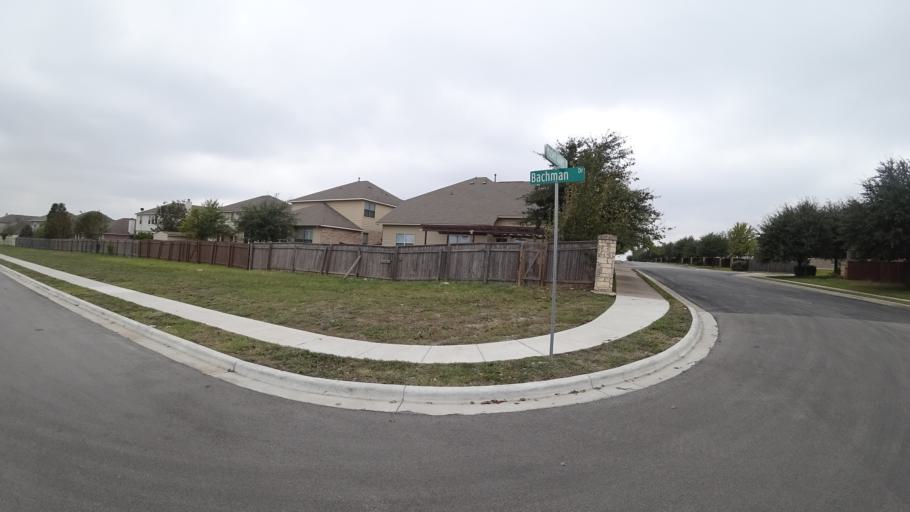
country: US
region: Texas
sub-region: Travis County
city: Pflugerville
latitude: 30.3723
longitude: -97.6480
